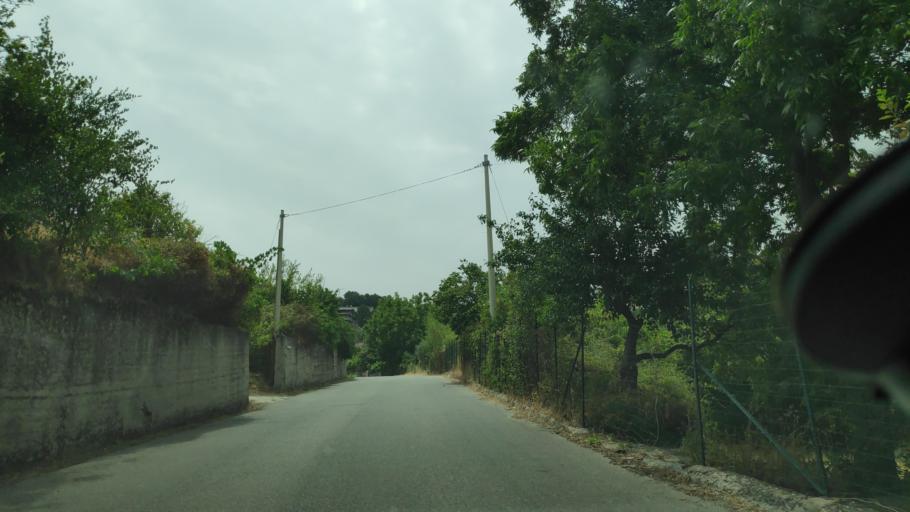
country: IT
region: Calabria
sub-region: Provincia di Catanzaro
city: Davoli
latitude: 38.6521
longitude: 16.4885
